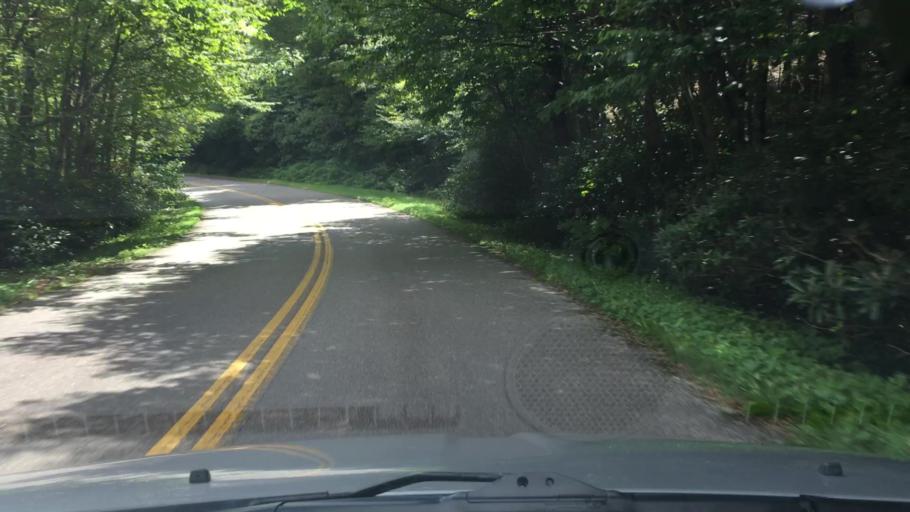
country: US
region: North Carolina
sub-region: Buncombe County
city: Black Mountain
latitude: 35.7036
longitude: -82.2647
